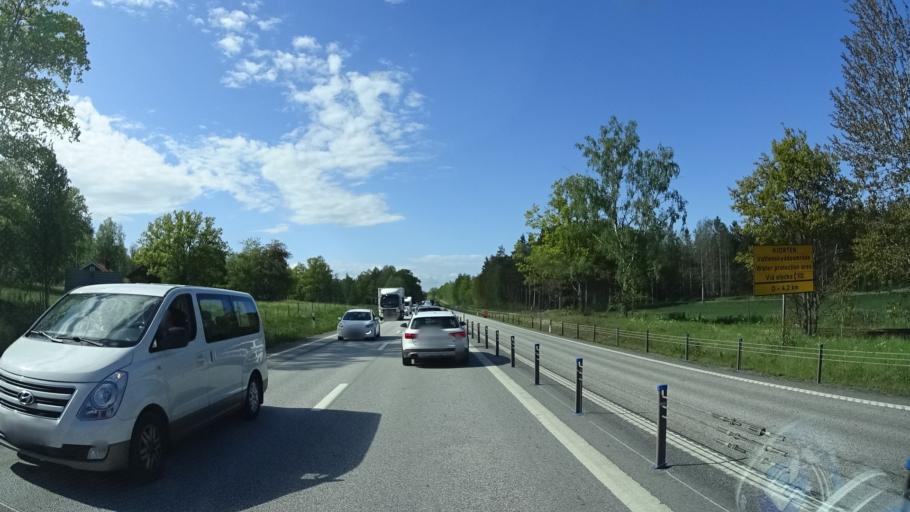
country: SE
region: Kalmar
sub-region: Vasterviks Kommun
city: Vaestervik
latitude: 57.7836
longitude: 16.5314
